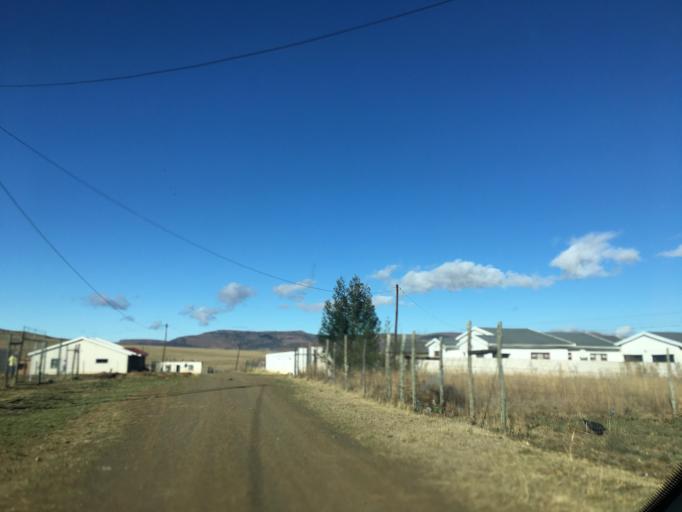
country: ZA
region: Eastern Cape
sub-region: Chris Hani District Municipality
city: Cala
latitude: -31.5396
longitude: 27.6973
